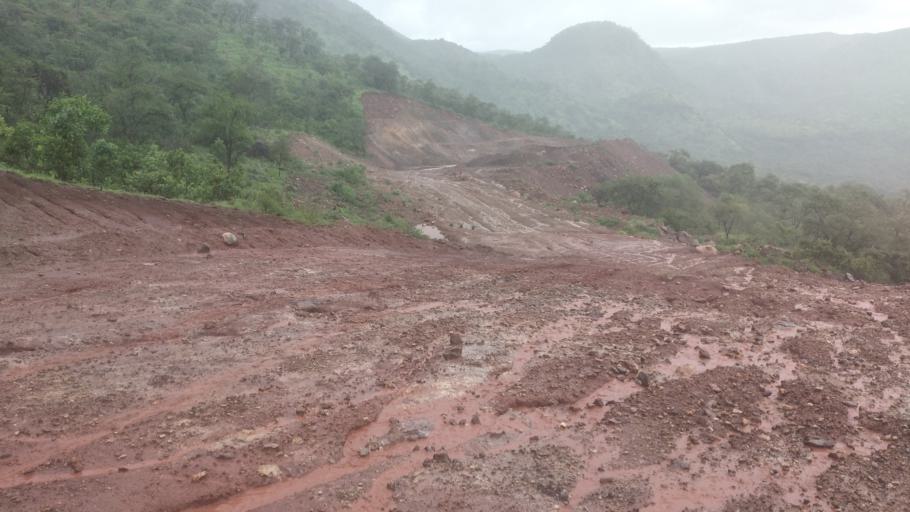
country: ET
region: Southern Nations, Nationalities, and People's Region
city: Areka
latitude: 7.6101
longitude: 37.5121
